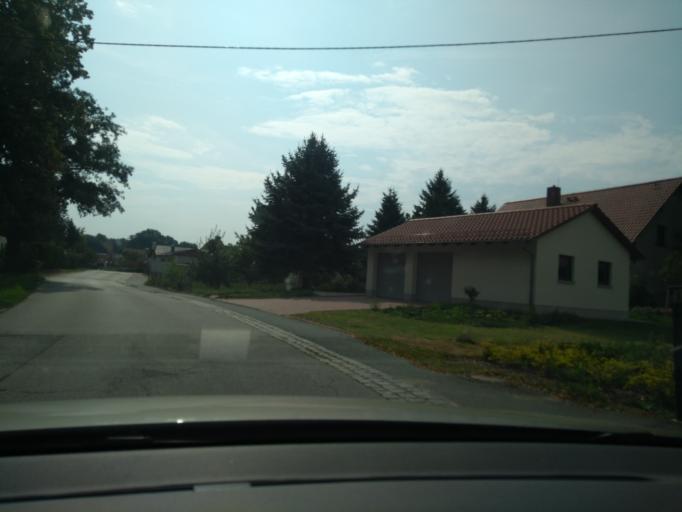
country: DE
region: Saxony
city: Markersdorf
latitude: 51.1379
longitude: 14.8775
